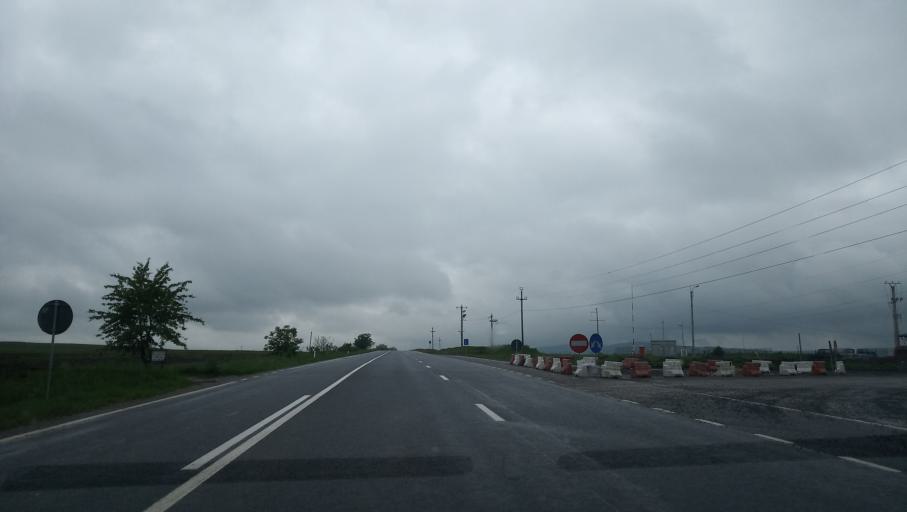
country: RO
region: Alba
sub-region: Comuna Cut
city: Cut
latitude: 45.9179
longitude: 23.7070
